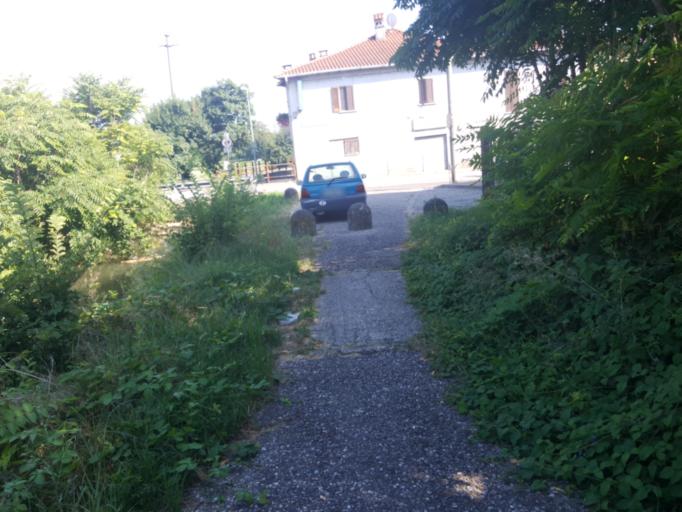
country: IT
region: Lombardy
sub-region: Citta metropolitana di Milano
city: Pieve Emanuele
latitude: 45.3621
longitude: 9.2061
